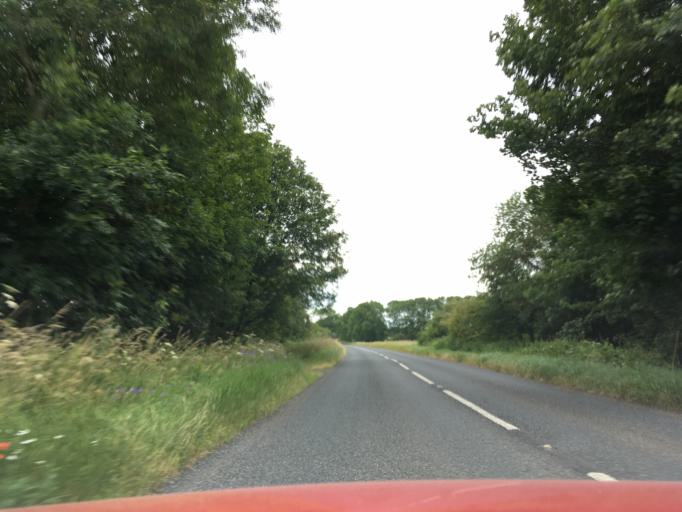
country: GB
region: England
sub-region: Gloucestershire
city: Westfield
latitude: 51.8906
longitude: -1.8653
